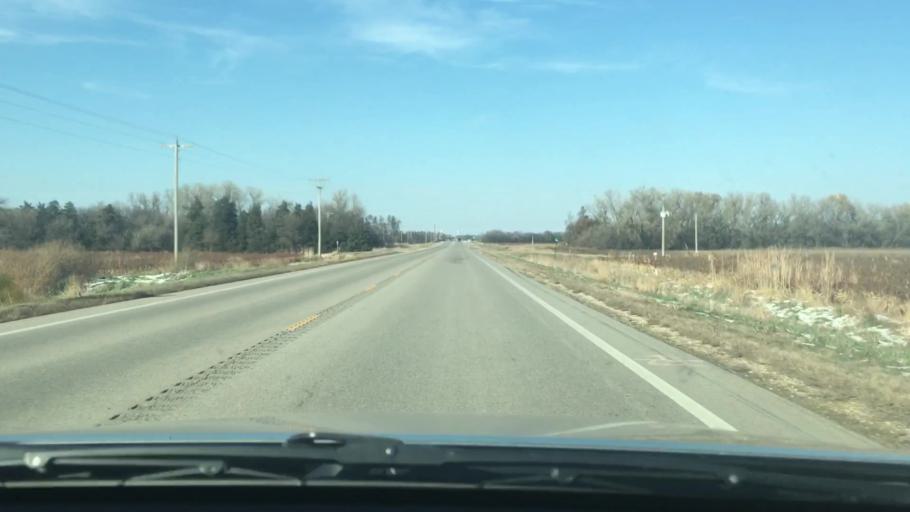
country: US
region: Kansas
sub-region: Rice County
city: Lyons
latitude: 38.3030
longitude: -98.2019
